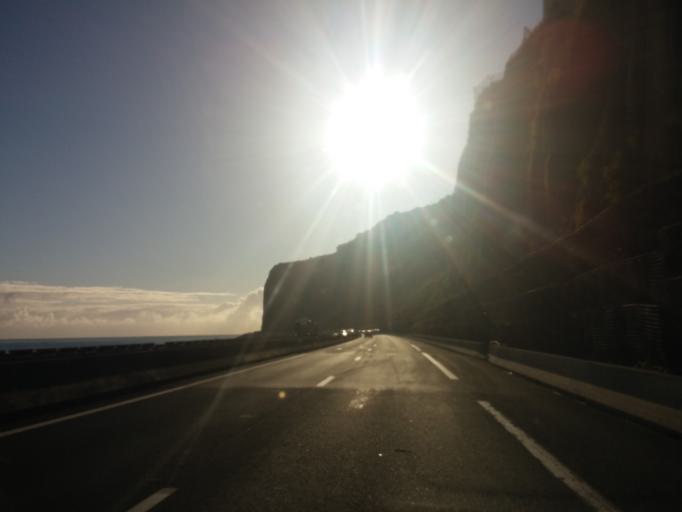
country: RE
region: Reunion
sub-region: Reunion
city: La Possession
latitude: -20.9088
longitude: 55.3593
